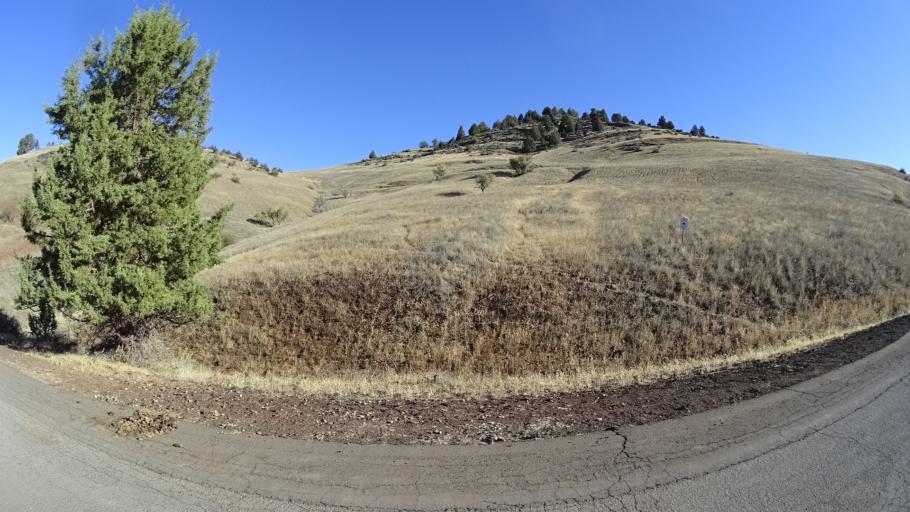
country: US
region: California
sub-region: Siskiyou County
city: Montague
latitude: 41.9668
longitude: -122.4324
